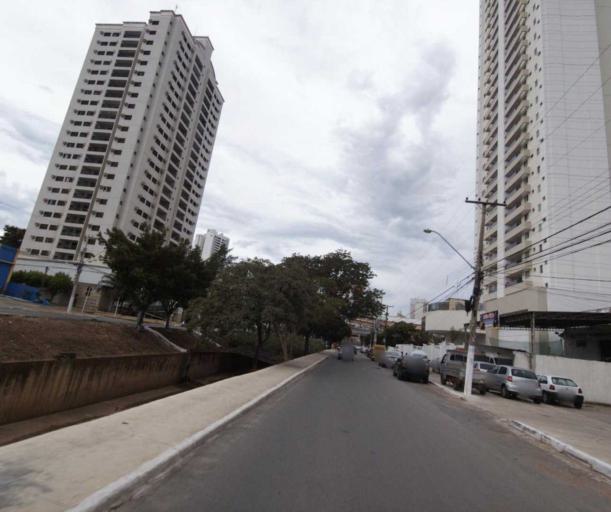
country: BR
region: Mato Grosso
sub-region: Cuiaba
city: Cuiaba
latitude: -15.6150
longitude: -56.0754
